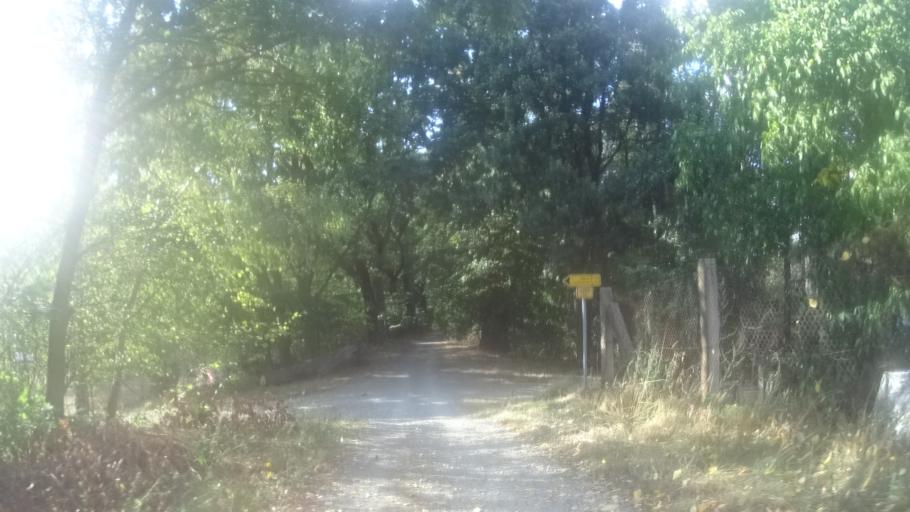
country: CZ
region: Kralovehradecky
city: Trebechovice pod Orebem
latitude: 50.1874
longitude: 16.0100
